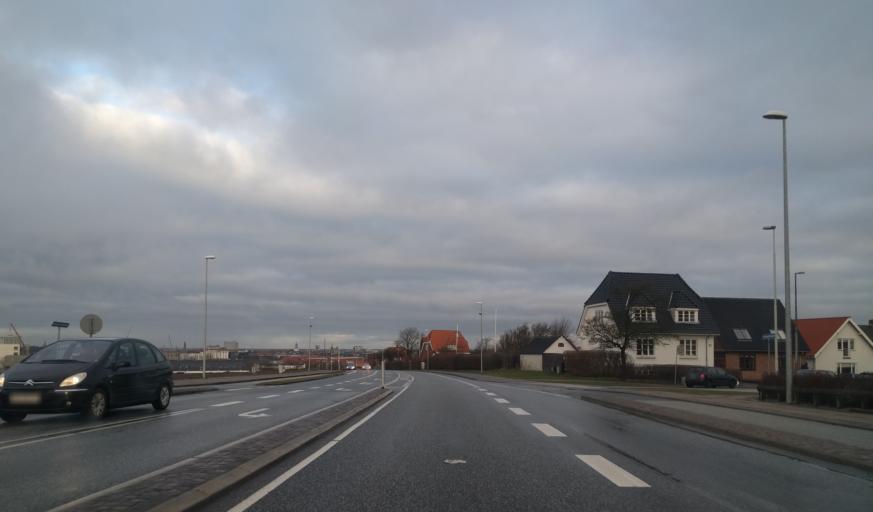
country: DK
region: North Denmark
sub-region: Alborg Kommune
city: Aalborg
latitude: 57.0331
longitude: 9.9427
